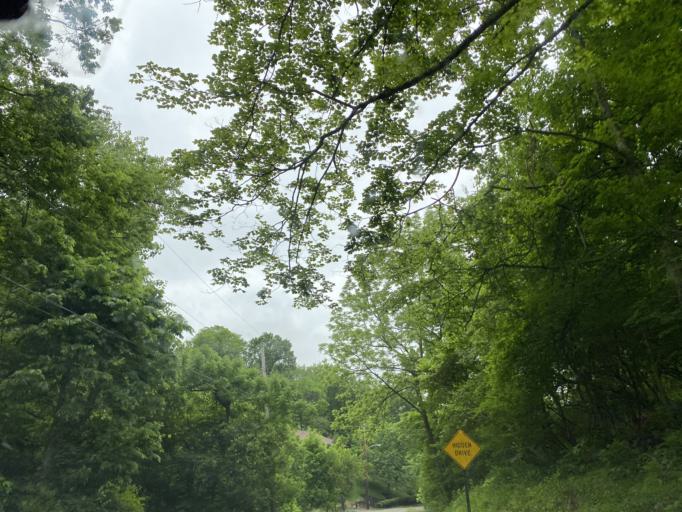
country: US
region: Kentucky
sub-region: Campbell County
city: Dayton
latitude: 39.1022
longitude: -84.4577
